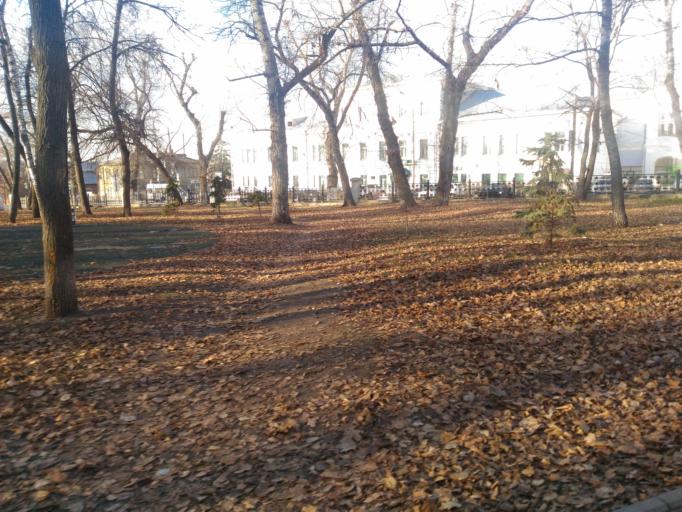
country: RU
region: Ulyanovsk
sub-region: Ulyanovskiy Rayon
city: Ulyanovsk
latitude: 54.3103
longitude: 48.3799
